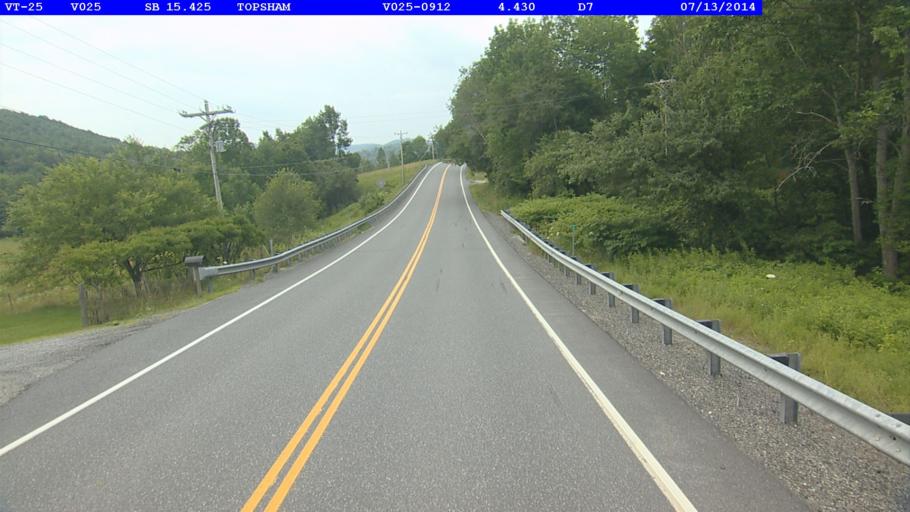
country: US
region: Vermont
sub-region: Orange County
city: Chelsea
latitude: 44.1136
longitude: -72.3150
